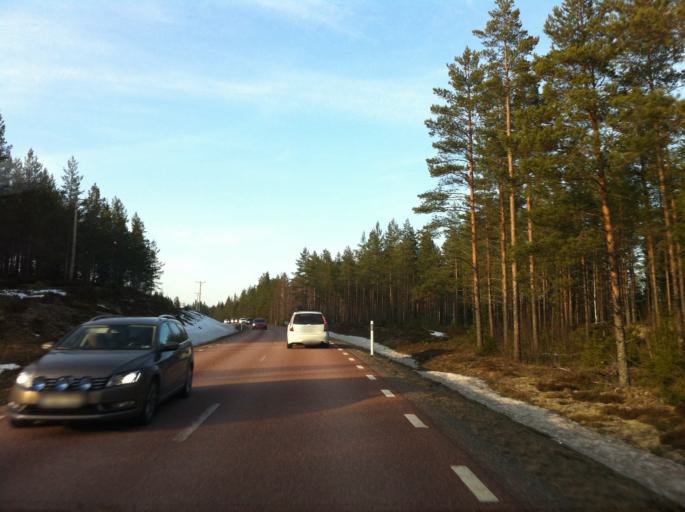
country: SE
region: Vaermland
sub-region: Filipstads Kommun
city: Lesjofors
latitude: 60.1854
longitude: 14.1964
